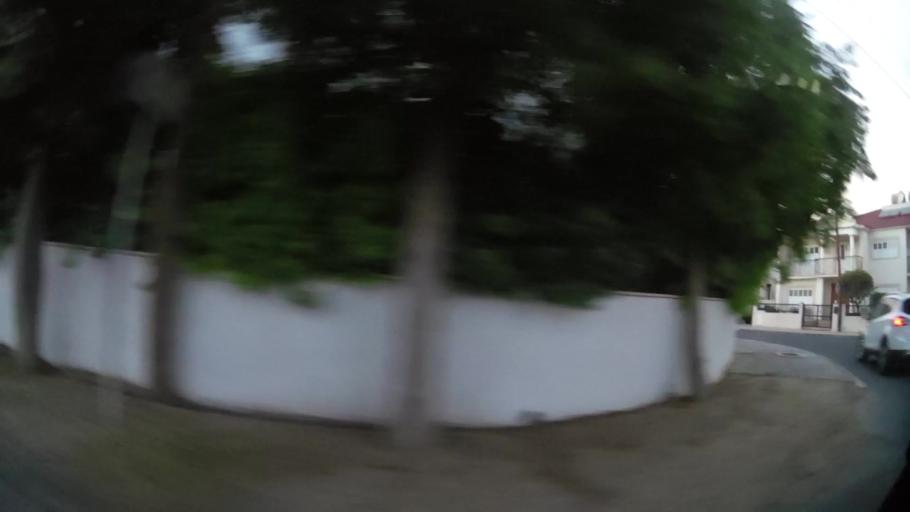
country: CY
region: Lefkosia
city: Nicosia
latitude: 35.1591
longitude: 33.3313
